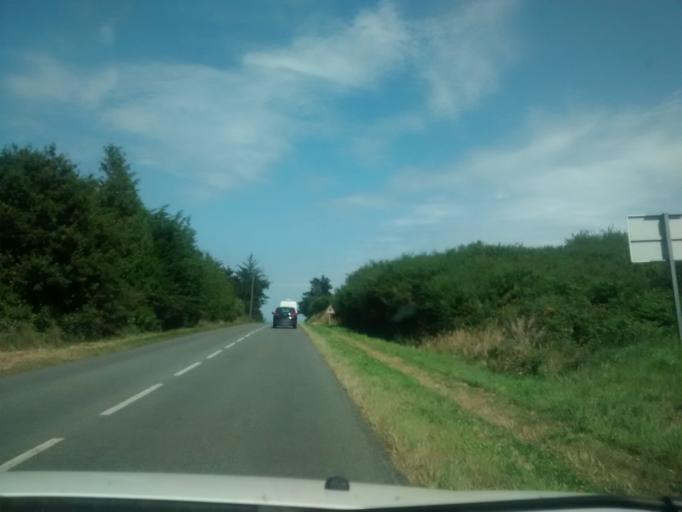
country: FR
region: Brittany
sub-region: Departement d'Ille-et-Vilaine
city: Cancale
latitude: 48.6877
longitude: -1.8517
